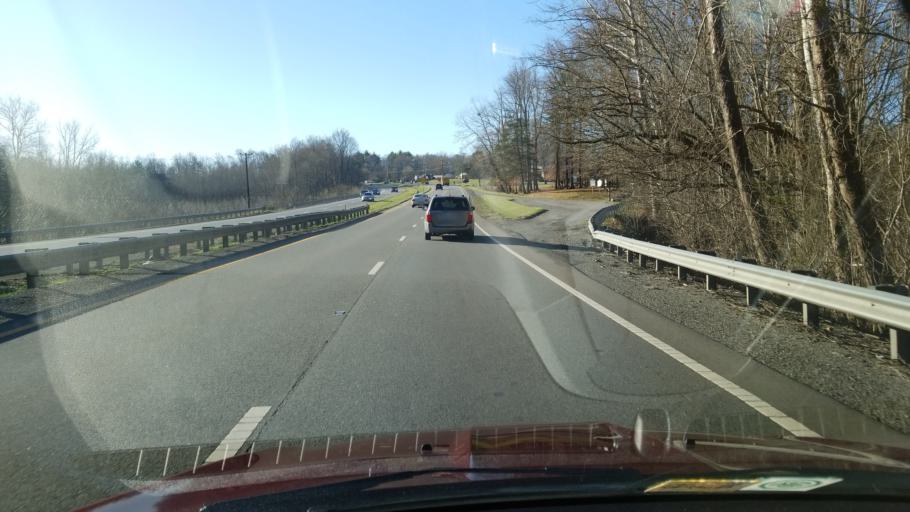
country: US
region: Virginia
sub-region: Franklin County
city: Rocky Mount
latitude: 37.0538
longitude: -79.8822
